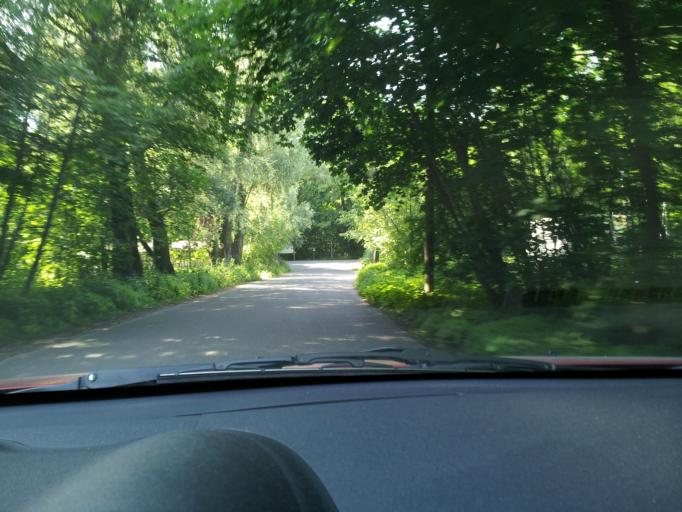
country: LV
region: Riga
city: Daugavgriva
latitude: 57.0617
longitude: 24.0549
